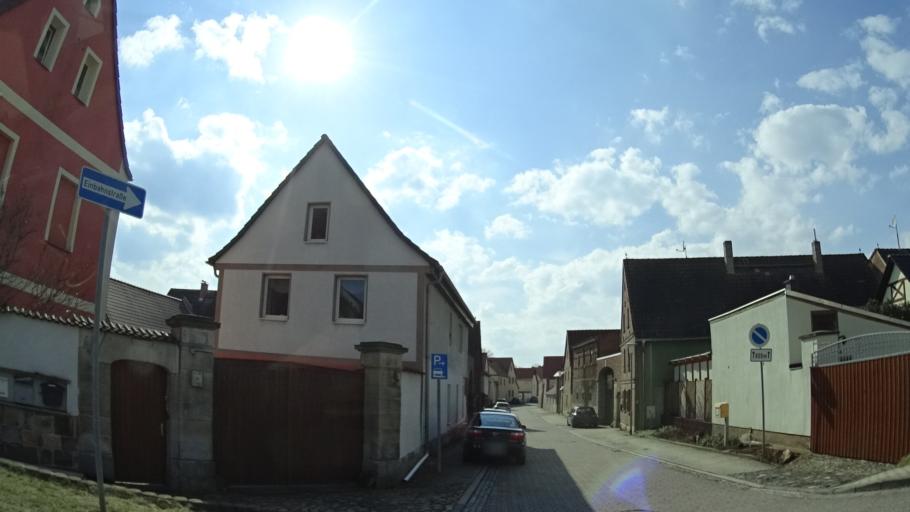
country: DE
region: Saxony-Anhalt
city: Prittitz
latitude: 51.1504
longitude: 11.9294
